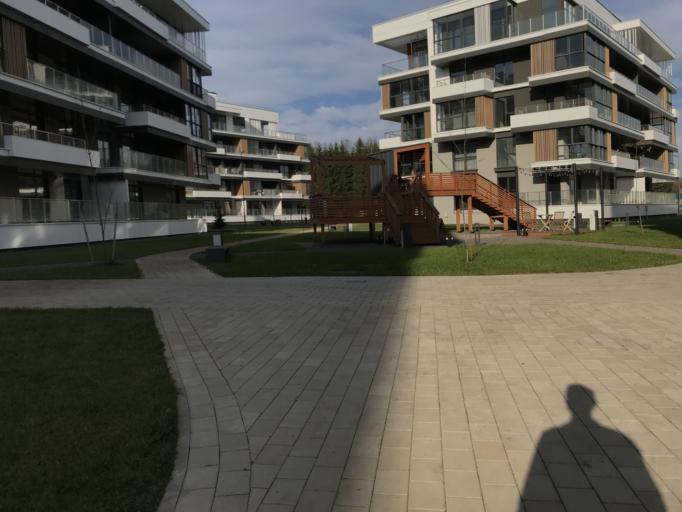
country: BY
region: Minsk
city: Khatsyezhyna
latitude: 53.9470
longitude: 27.3314
